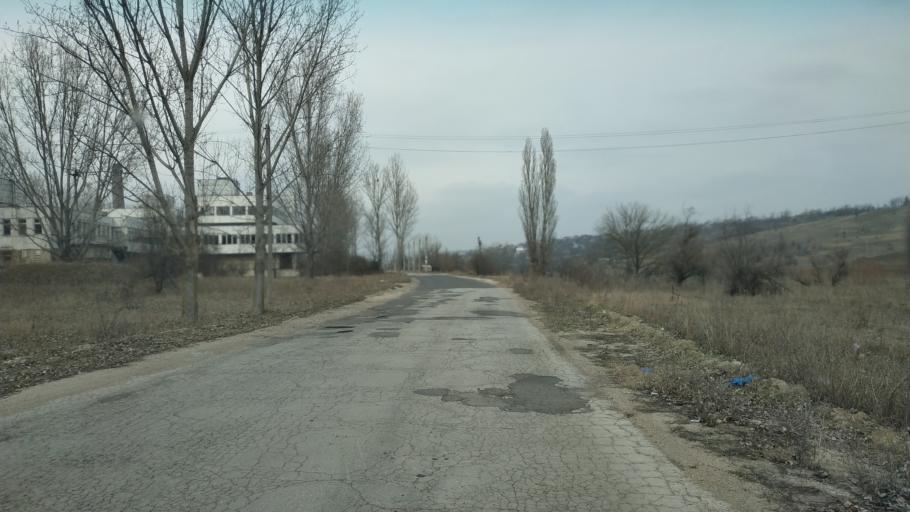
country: MD
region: Chisinau
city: Singera
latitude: 46.9020
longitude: 29.0200
